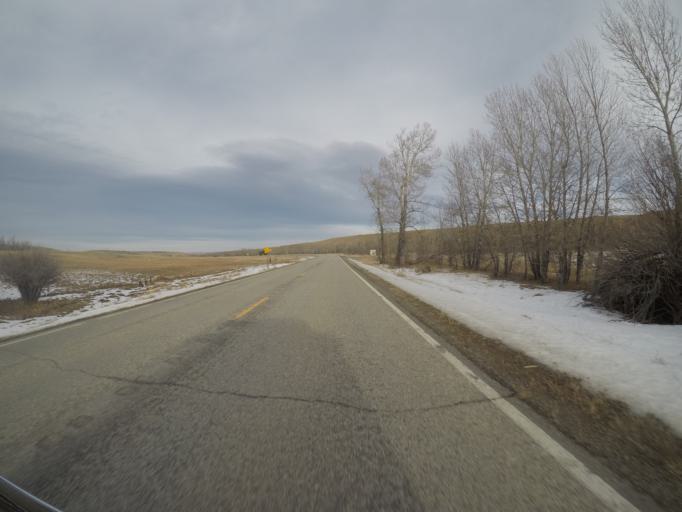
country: US
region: Montana
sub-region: Stillwater County
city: Absarokee
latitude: 45.4146
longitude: -109.4756
